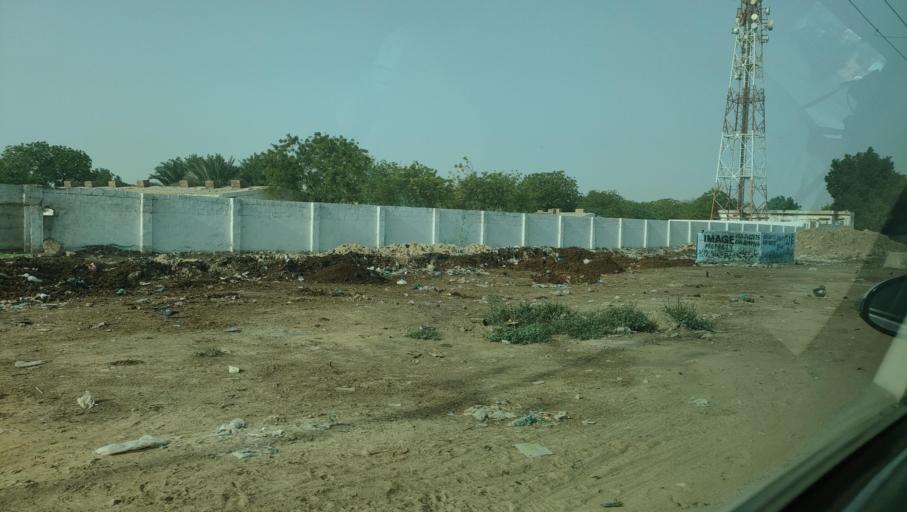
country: PK
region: Sindh
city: Malir Cantonment
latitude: 24.9350
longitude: 67.1720
